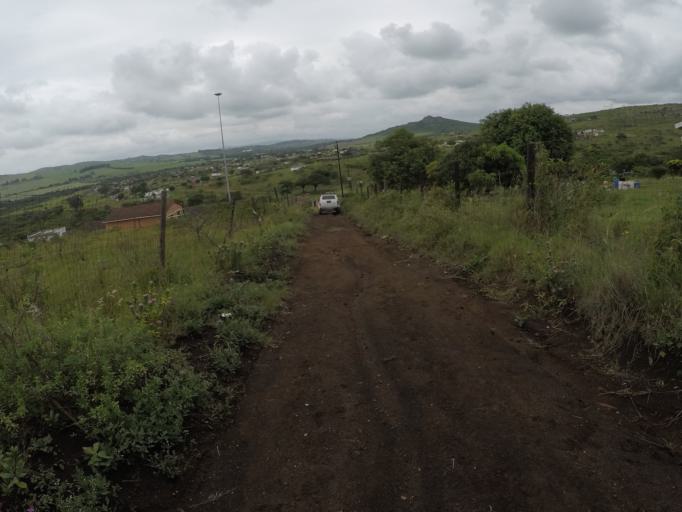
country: ZA
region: KwaZulu-Natal
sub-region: uThungulu District Municipality
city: Empangeni
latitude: -28.7088
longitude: 31.8504
